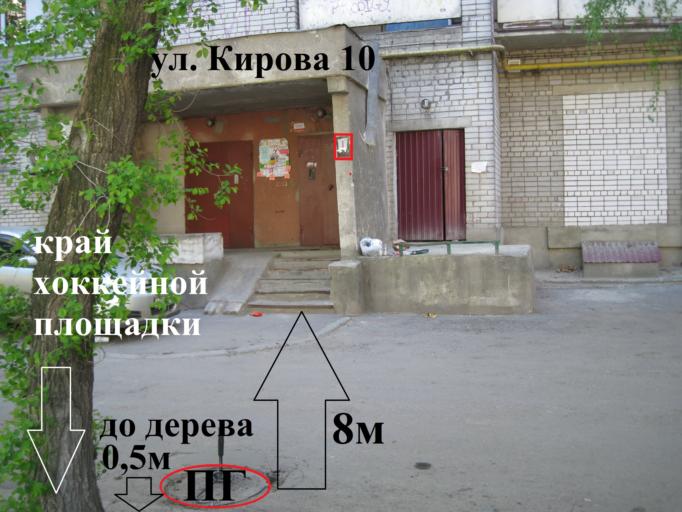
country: RU
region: Voronezj
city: Voronezh
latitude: 51.6582
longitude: 39.1914
